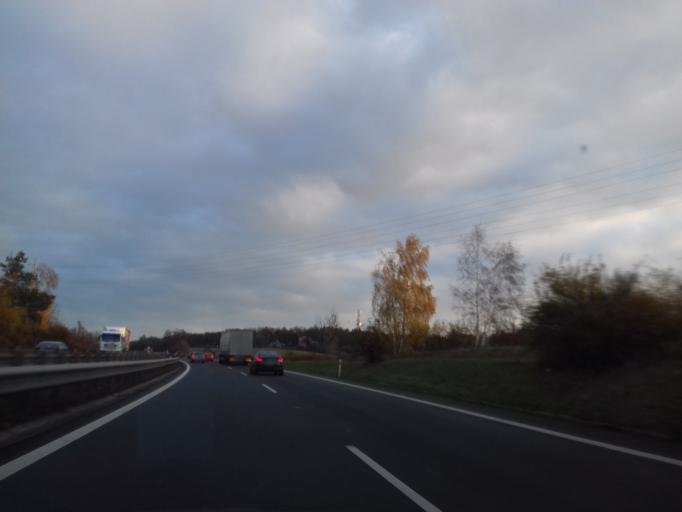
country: CZ
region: Olomoucky
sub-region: Okres Prostejov
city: Prostejov
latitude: 49.4915
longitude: 17.1416
